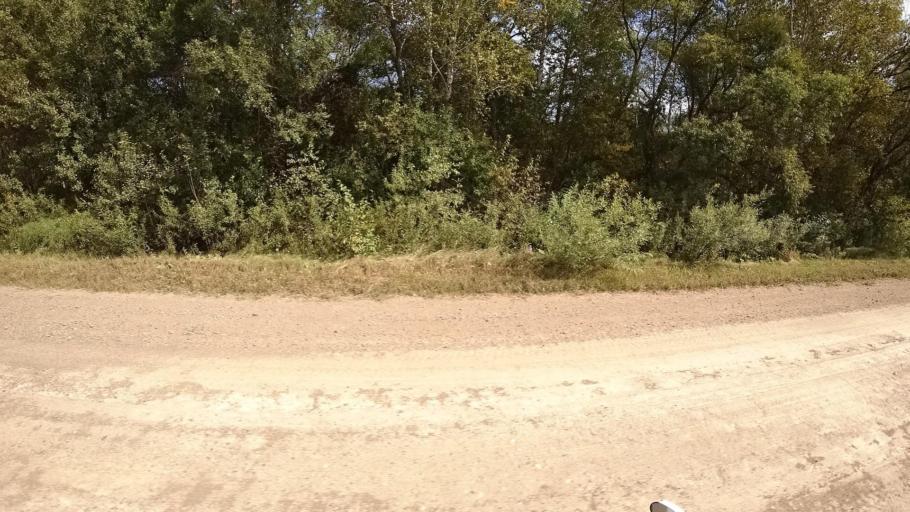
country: RU
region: Primorskiy
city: Yakovlevka
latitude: 44.7219
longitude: 133.6142
